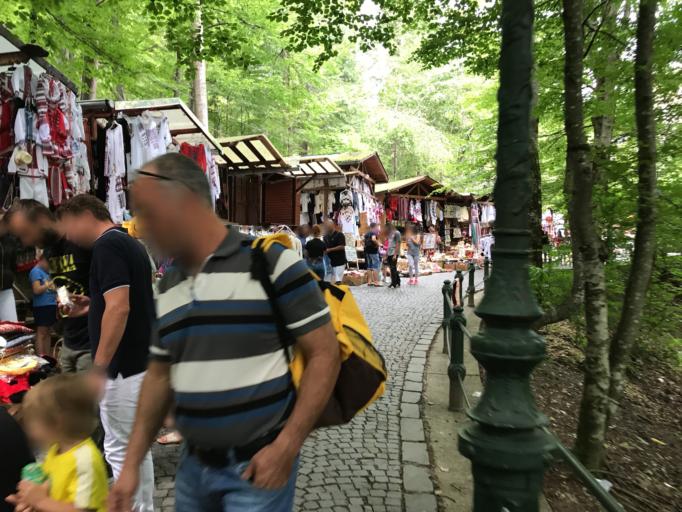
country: RO
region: Prahova
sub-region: Oras Sinaia
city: Sinaia
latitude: 45.3583
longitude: 25.5444
